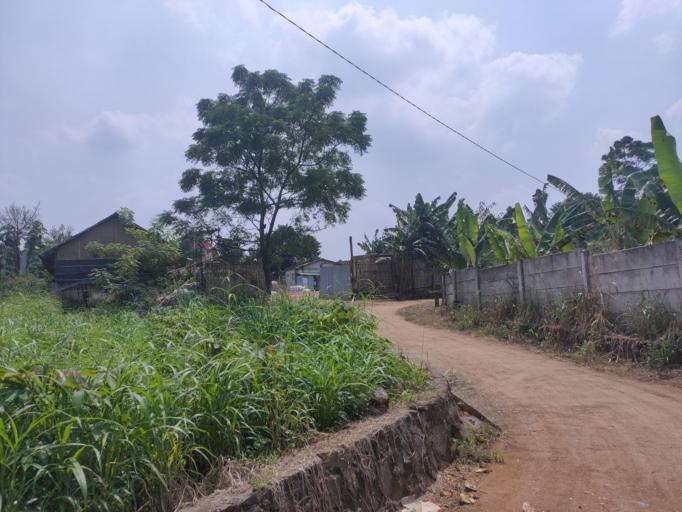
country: ID
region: West Java
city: Parung
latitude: -6.3988
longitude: 106.7197
